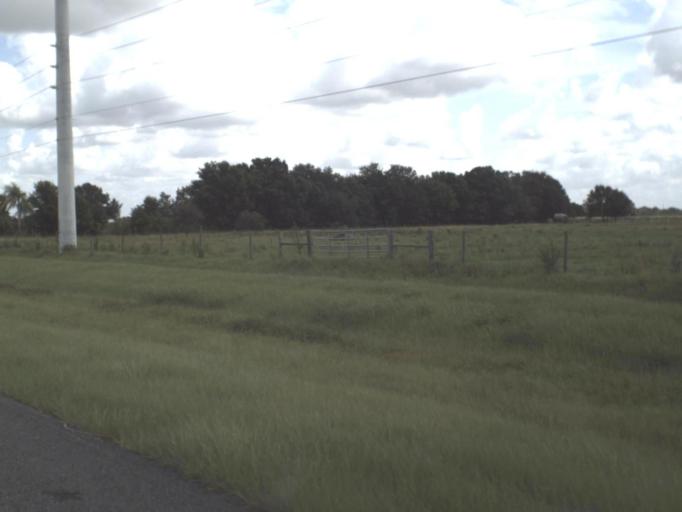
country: US
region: Florida
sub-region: Charlotte County
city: Harbour Heights
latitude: 27.0694
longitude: -81.9580
